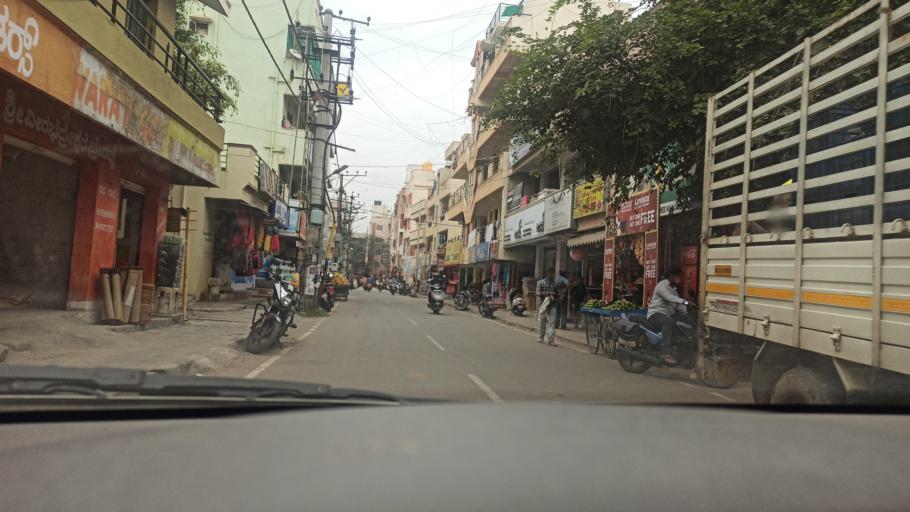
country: IN
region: Karnataka
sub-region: Bangalore Urban
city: Bangalore
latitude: 12.9915
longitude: 77.6801
